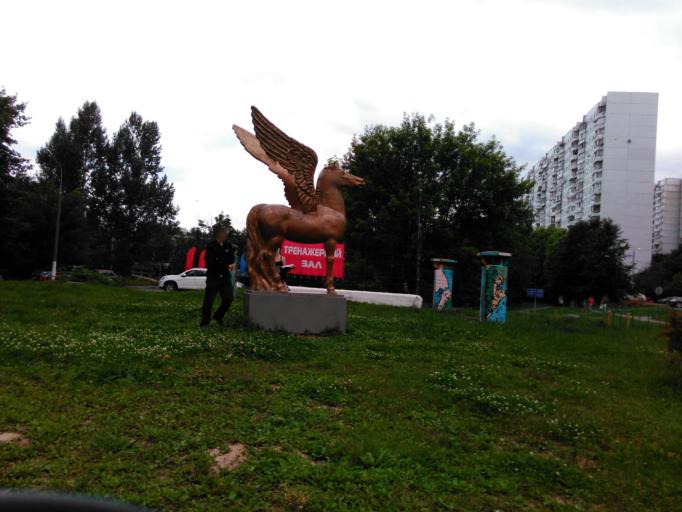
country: RU
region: Moscow
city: Yasenevo
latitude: 55.6318
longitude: 37.5236
